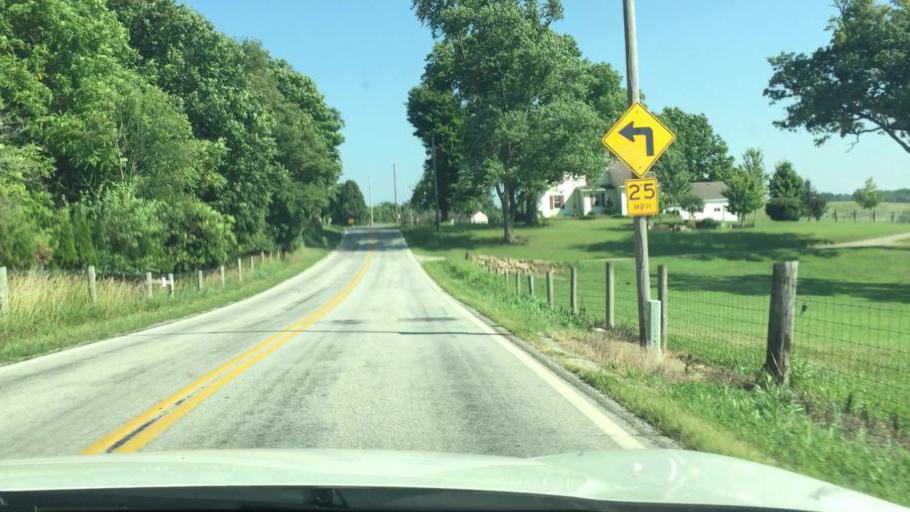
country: US
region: Ohio
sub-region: Clark County
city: Northridge
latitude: 39.9843
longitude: -83.6826
